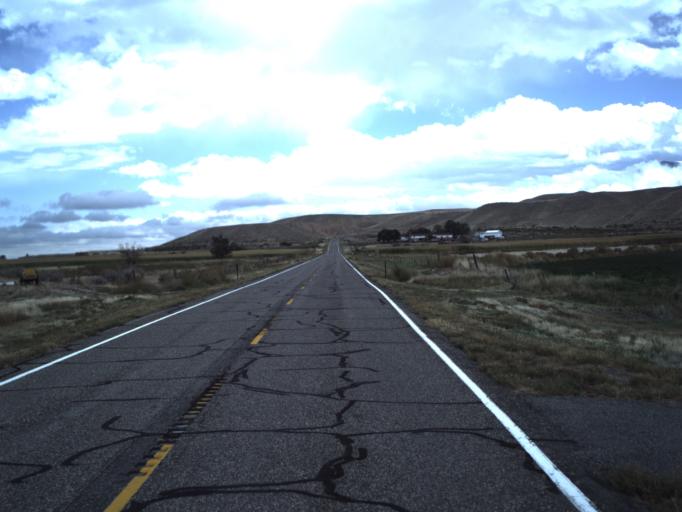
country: US
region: Utah
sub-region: Sevier County
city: Monroe
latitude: 38.6286
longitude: -112.1976
